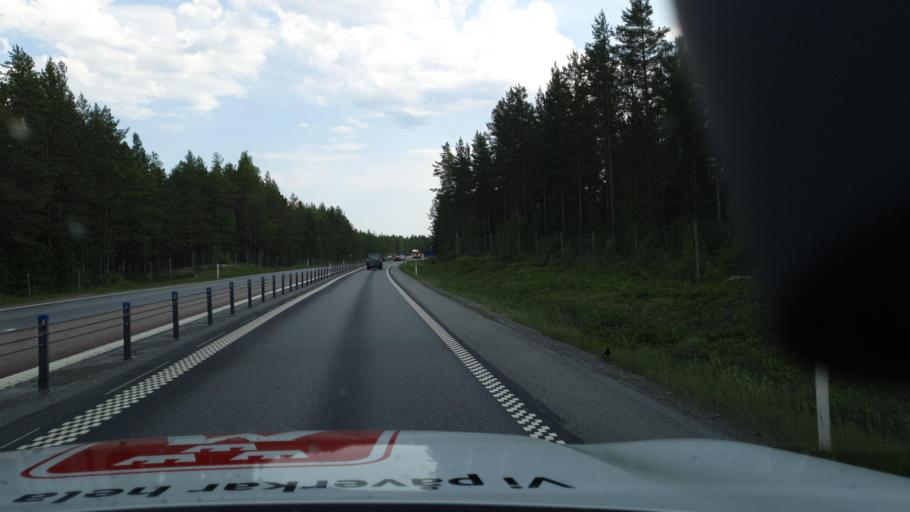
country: SE
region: Vaesterbotten
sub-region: Skelleftea Kommun
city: Burea
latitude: 64.6344
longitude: 21.1730
